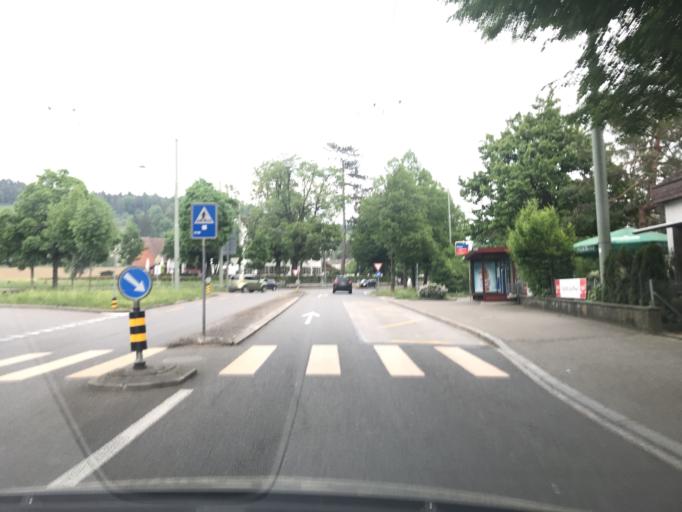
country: CH
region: Zurich
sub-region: Bezirk Winterthur
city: Wuelflingen (Kreis 6) / Lindenplatz
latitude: 47.5109
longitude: 8.6977
